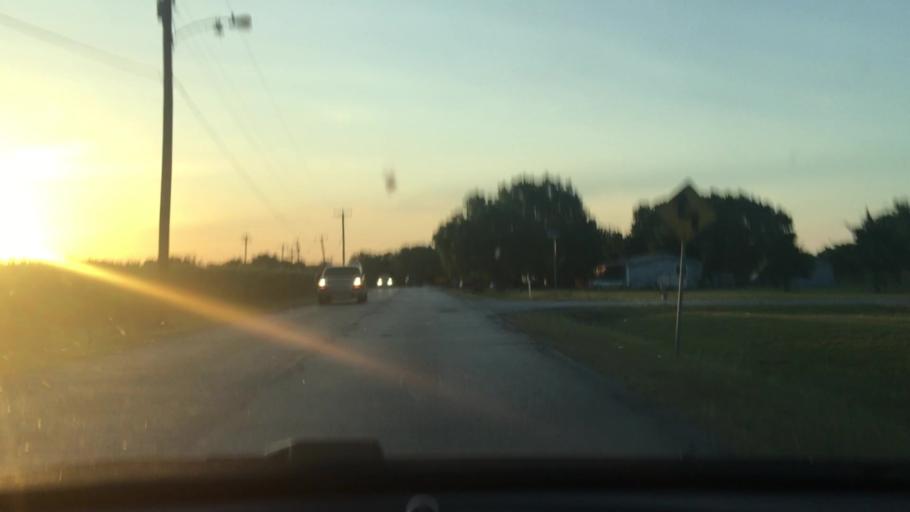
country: US
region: Texas
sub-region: Ellis County
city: Red Oak
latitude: 32.5607
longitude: -96.7901
